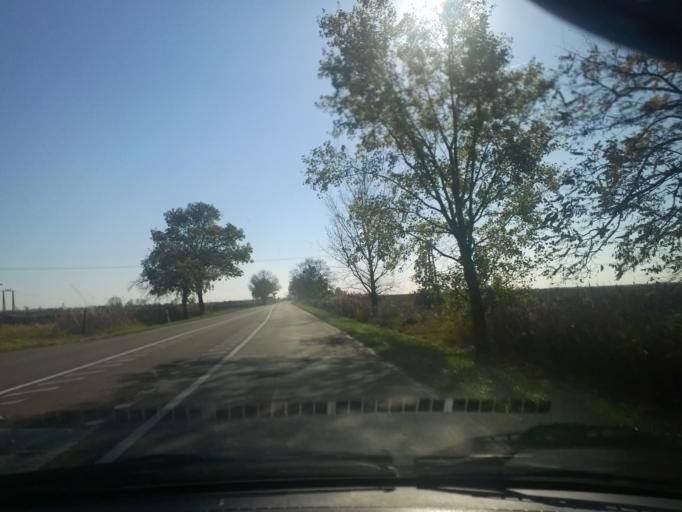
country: HU
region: Csongrad
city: Szentes
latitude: 46.5943
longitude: 20.2960
